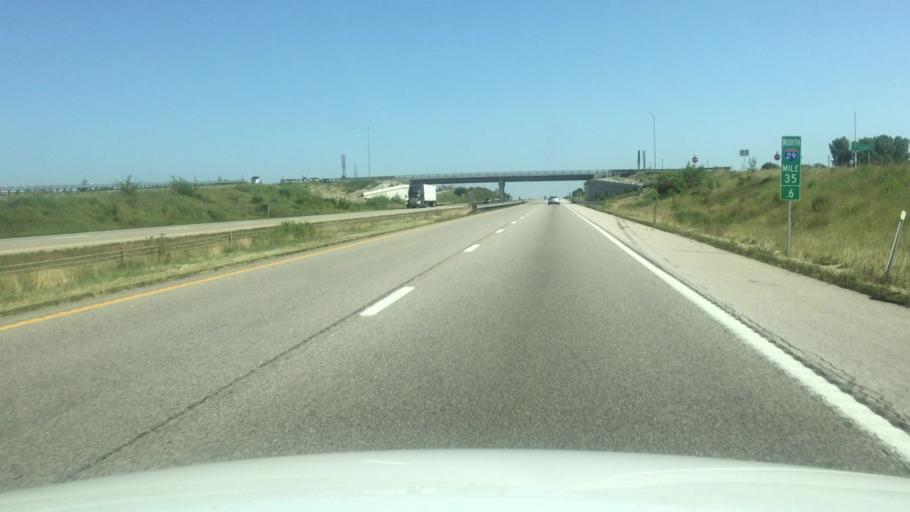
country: US
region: Kansas
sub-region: Doniphan County
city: Elwood
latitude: 39.5980
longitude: -94.7886
